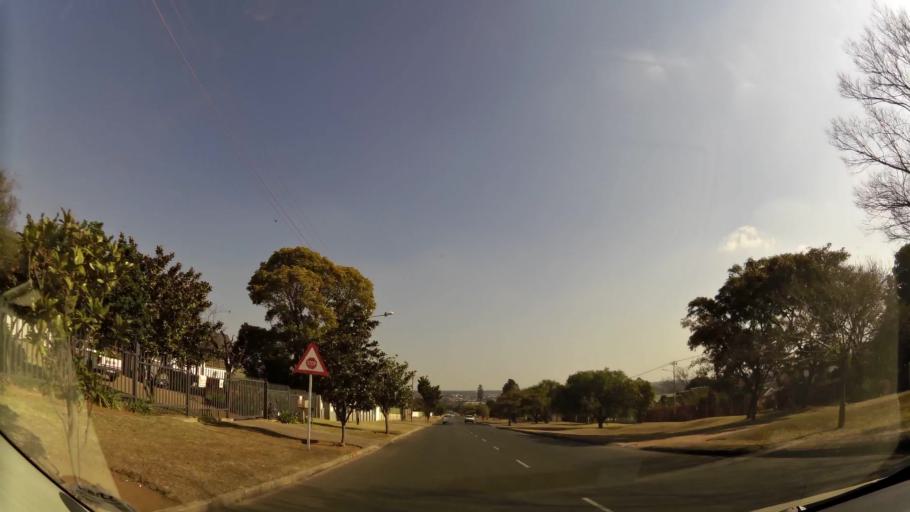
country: ZA
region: Gauteng
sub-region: West Rand District Municipality
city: Randfontein
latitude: -26.1573
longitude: 27.6965
